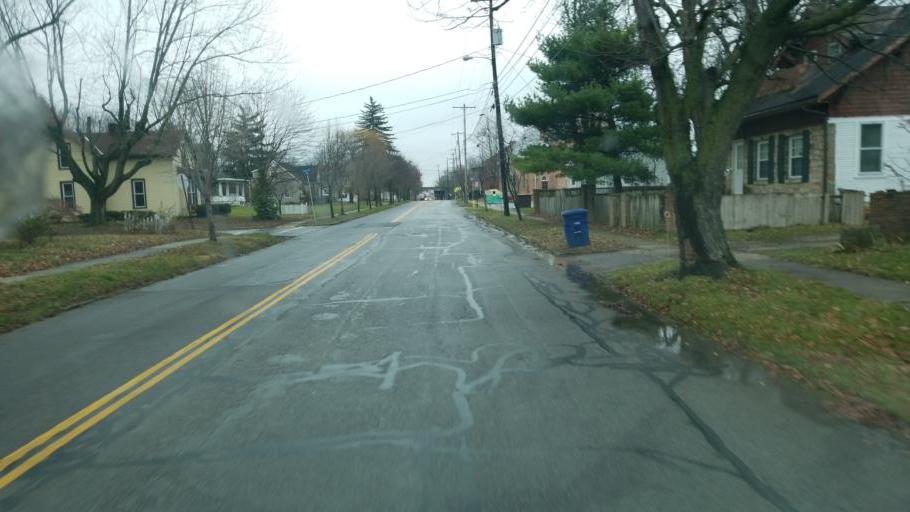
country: US
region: Ohio
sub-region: Delaware County
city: Delaware
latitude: 40.2988
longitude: -83.0511
